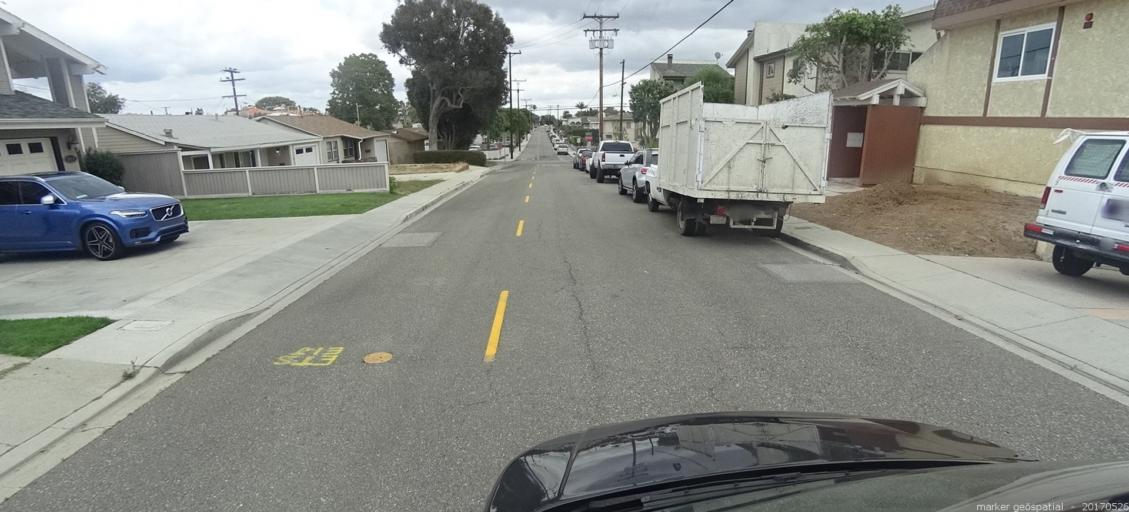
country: US
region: California
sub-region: Los Angeles County
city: Lawndale
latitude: 33.8794
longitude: -118.3652
